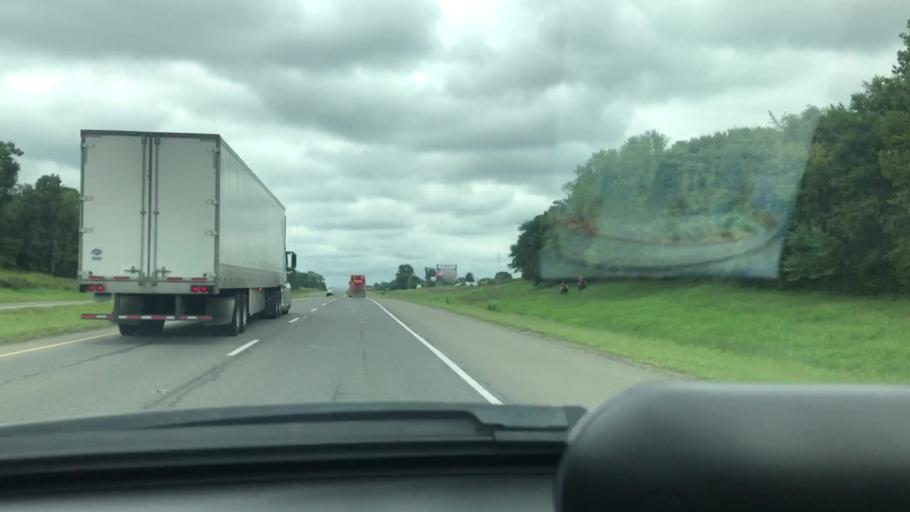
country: US
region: Oklahoma
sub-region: Muskogee County
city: Muskogee
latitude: 35.8225
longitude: -95.4026
